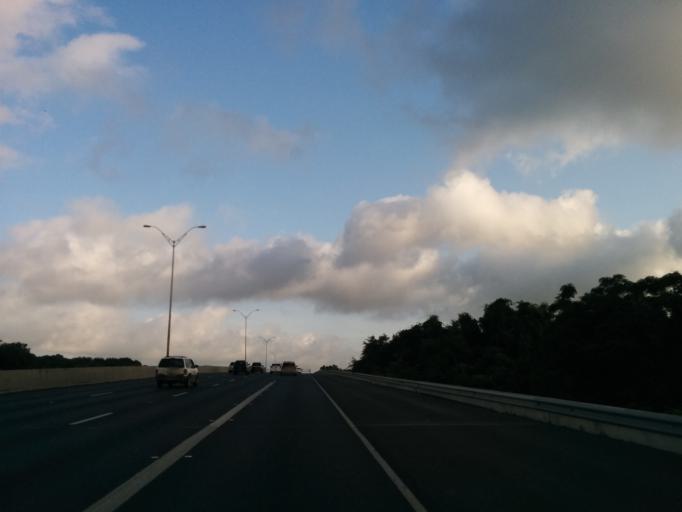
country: US
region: Texas
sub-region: Bexar County
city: Olmos Park
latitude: 29.4698
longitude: -98.4756
